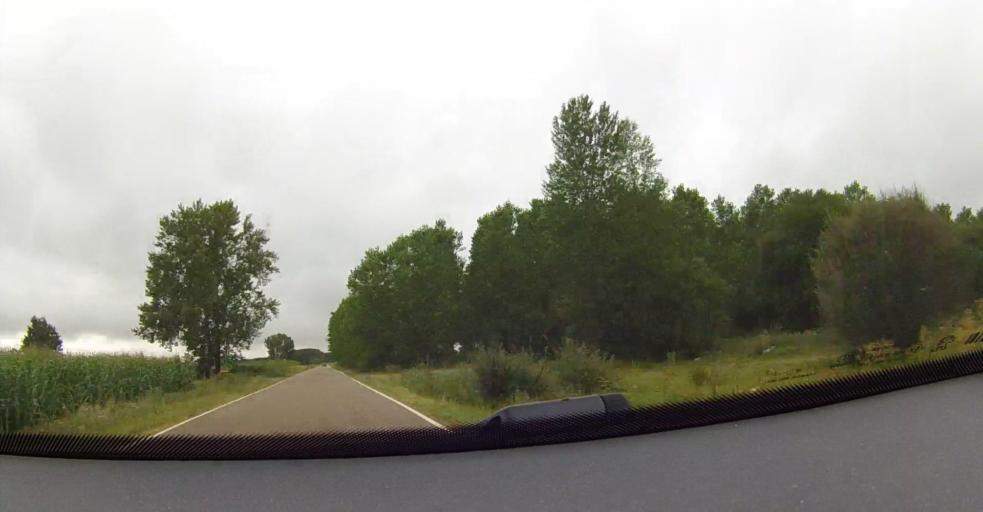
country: ES
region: Castille and Leon
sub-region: Provincia de Palencia
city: Pedrosa de la Vega
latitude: 42.4831
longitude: -4.7246
